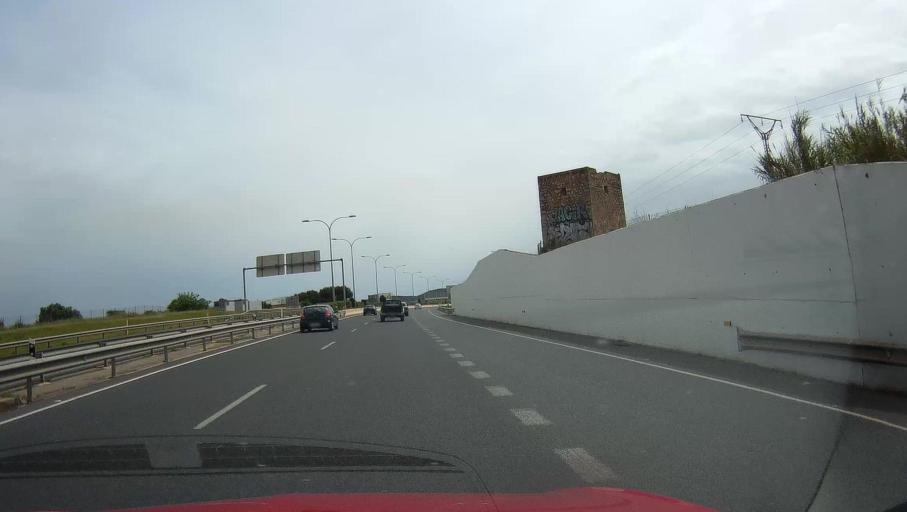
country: ES
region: Balearic Islands
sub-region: Illes Balears
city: Ibiza
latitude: 38.8928
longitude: 1.4007
